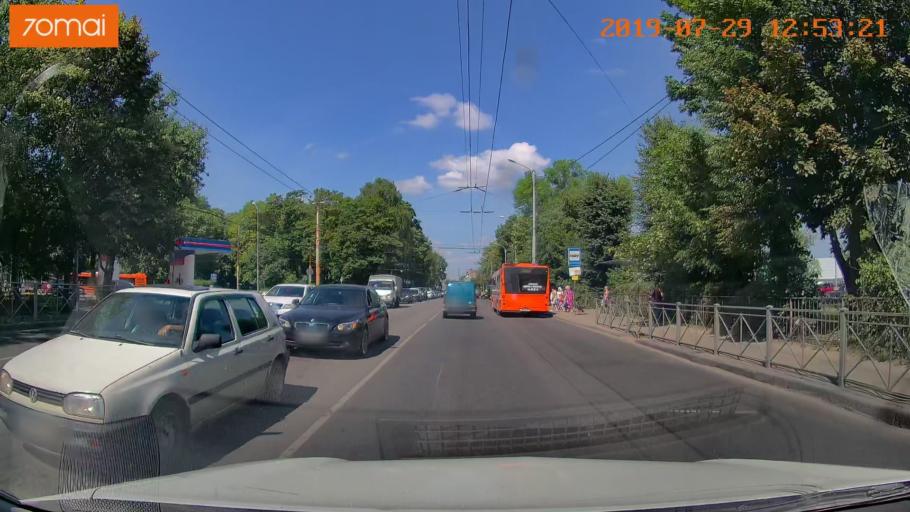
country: RU
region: Kaliningrad
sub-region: Gorod Kaliningrad
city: Kaliningrad
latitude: 54.6939
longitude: 20.5251
